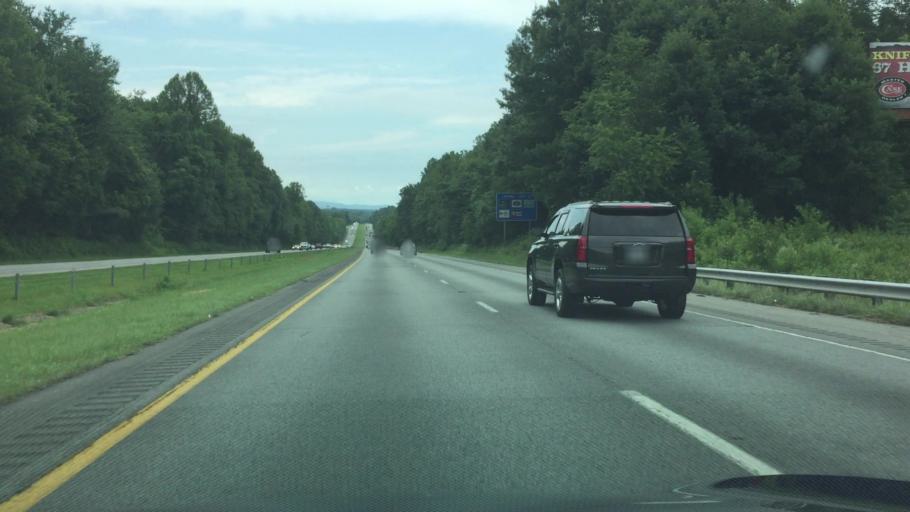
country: US
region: North Carolina
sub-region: Yadkin County
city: Jonesville
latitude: 36.2241
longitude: -80.8128
